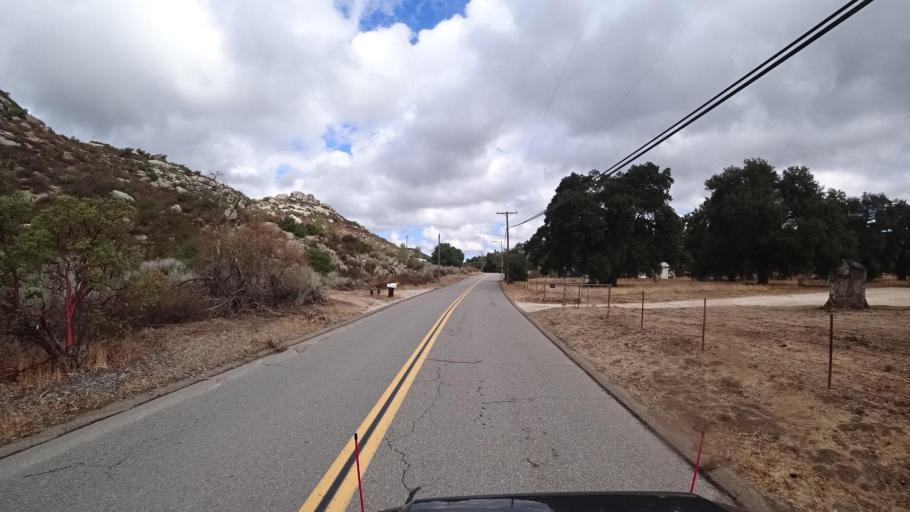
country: US
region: California
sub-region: San Diego County
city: Campo
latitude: 32.6475
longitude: -116.4233
